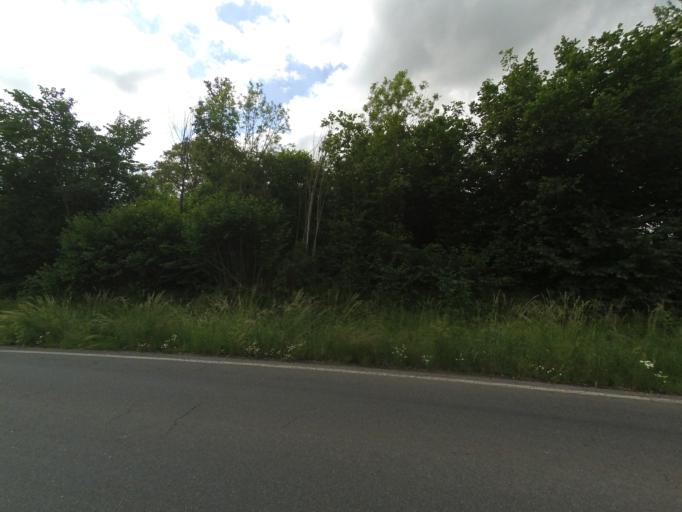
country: CZ
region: Plzensky
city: Straz
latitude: 49.6866
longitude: 12.8151
